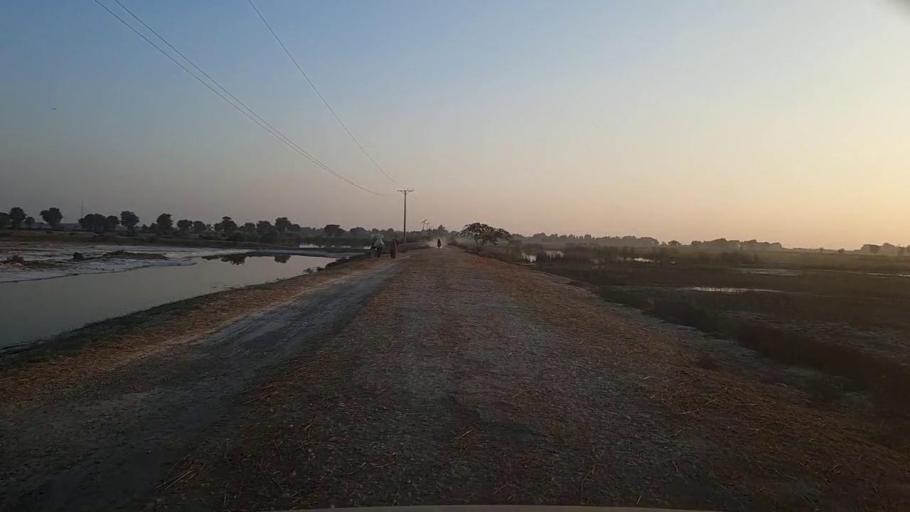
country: PK
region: Sindh
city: Khairpur Nathan Shah
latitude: 27.1653
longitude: 67.7323
